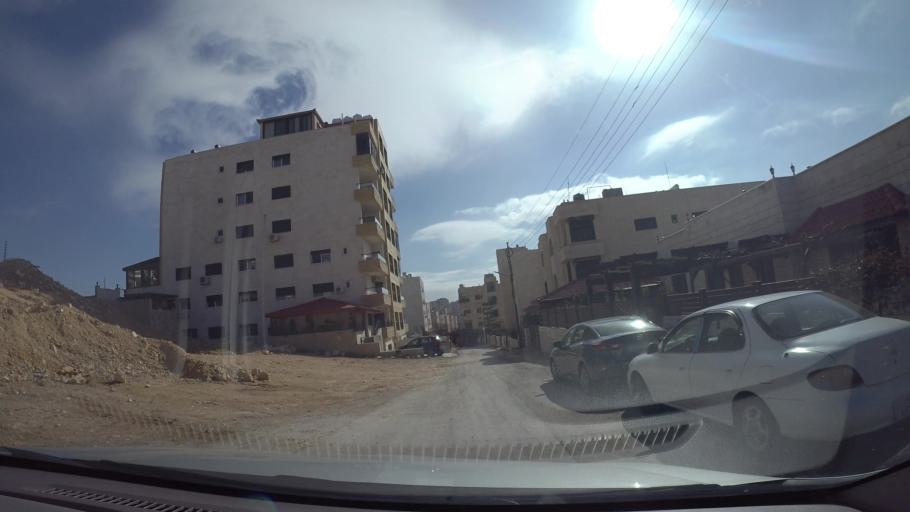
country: JO
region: Amman
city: Al Jubayhah
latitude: 32.0009
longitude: 35.8430
